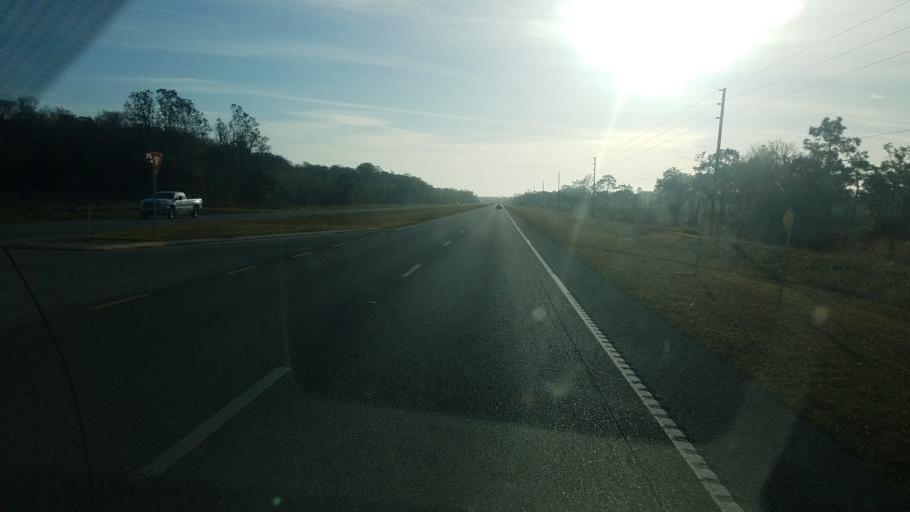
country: US
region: Florida
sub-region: Osceola County
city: Saint Cloud
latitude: 28.1357
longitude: -81.0306
